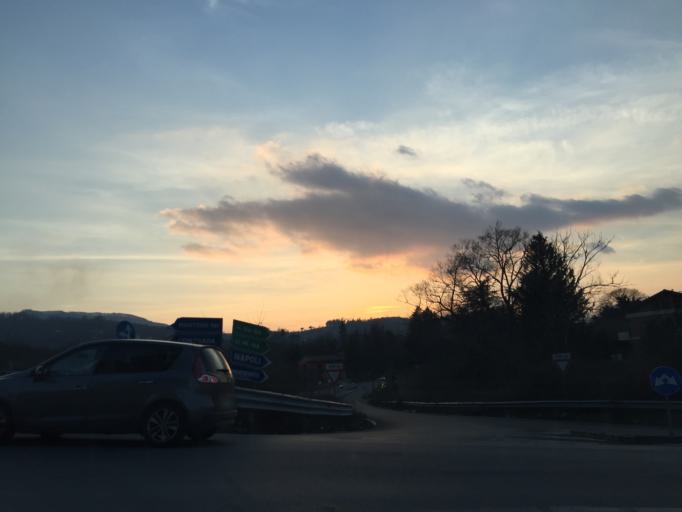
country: IT
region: Campania
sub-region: Provincia di Avellino
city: Avellino
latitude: 40.9001
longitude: 14.7984
